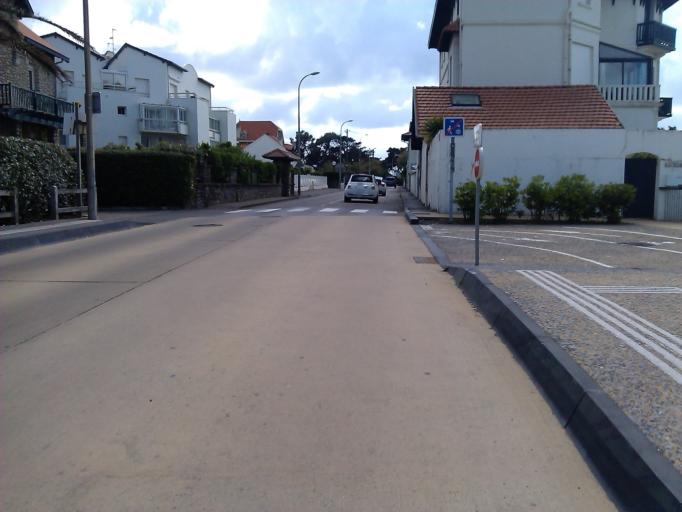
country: FR
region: Aquitaine
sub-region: Departement des Pyrenees-Atlantiques
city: Biarritz
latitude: 43.4936
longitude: -1.5456
